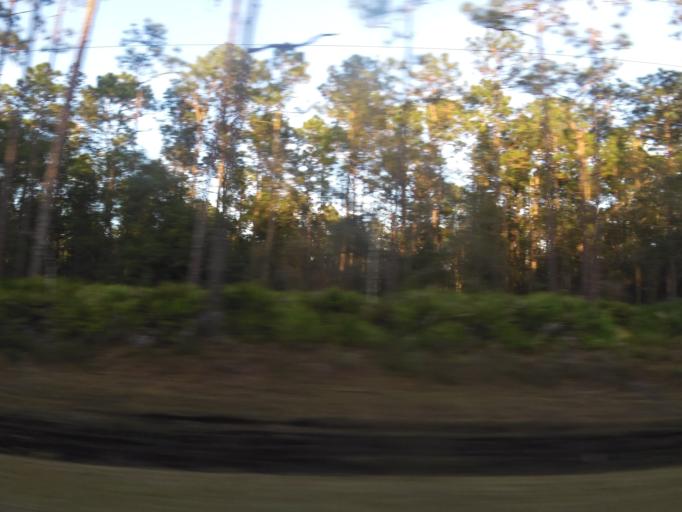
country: US
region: Florida
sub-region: Clay County
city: Green Cove Springs
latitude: 29.8738
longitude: -81.5496
